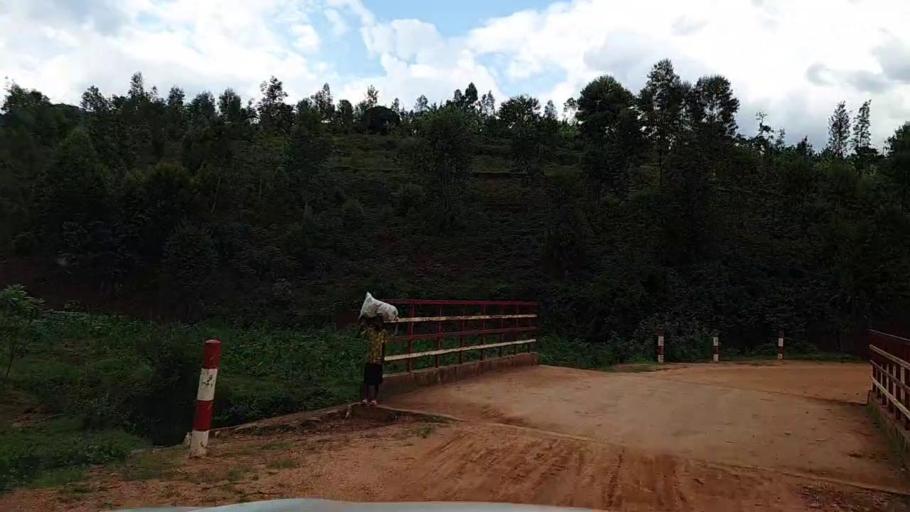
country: RW
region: Southern Province
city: Nyanza
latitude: -2.4004
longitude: 29.6771
